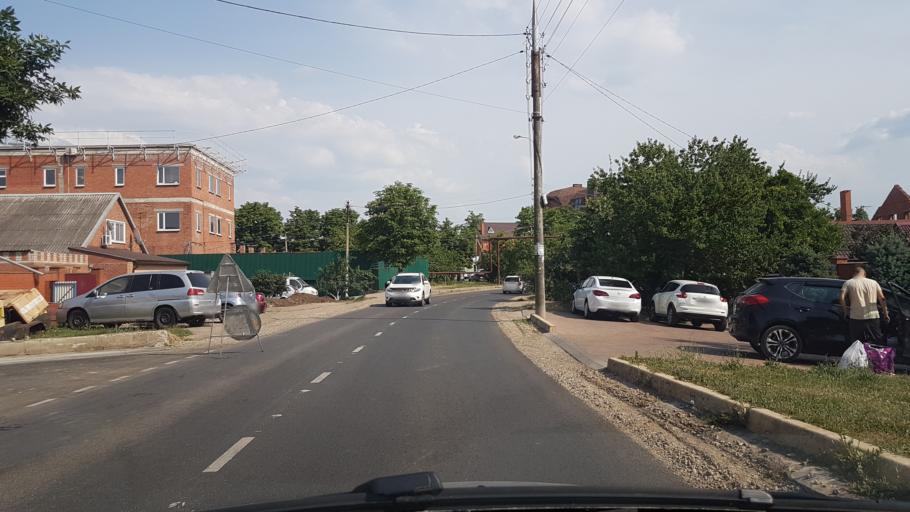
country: RU
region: Krasnodarskiy
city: Pashkovskiy
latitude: 45.0267
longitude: 39.1264
